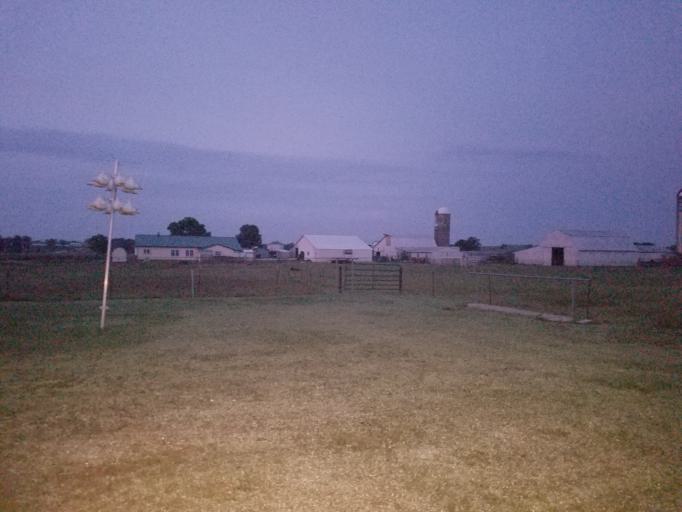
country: US
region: Oklahoma
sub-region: Mayes County
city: Chouteau
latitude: 36.1389
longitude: -95.3870
